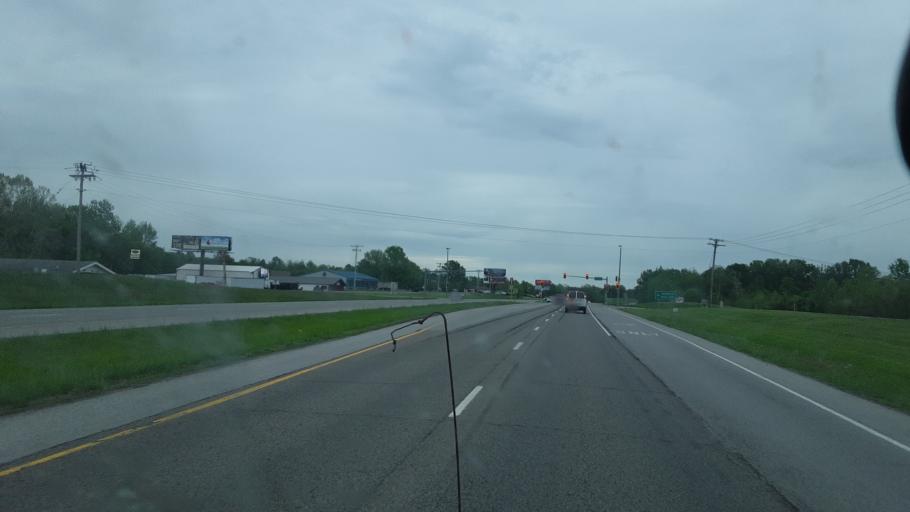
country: US
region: Illinois
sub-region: Jackson County
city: Murphysboro
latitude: 37.7621
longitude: -89.2823
